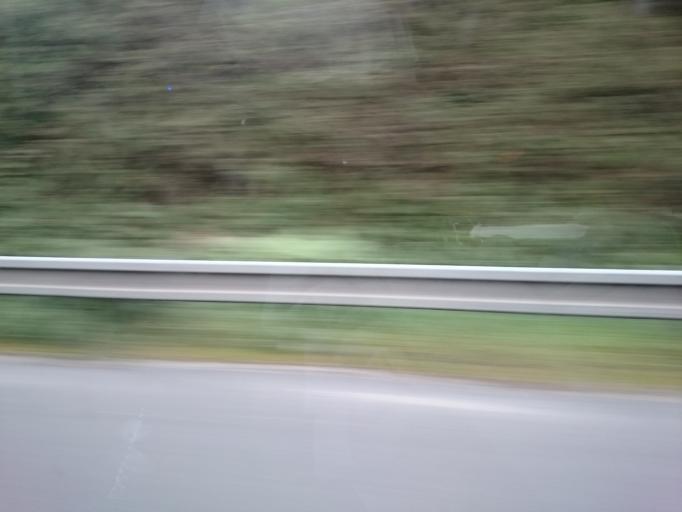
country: FR
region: Brittany
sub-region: Departement du Morbihan
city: Lorient
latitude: 47.7717
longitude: -3.3848
